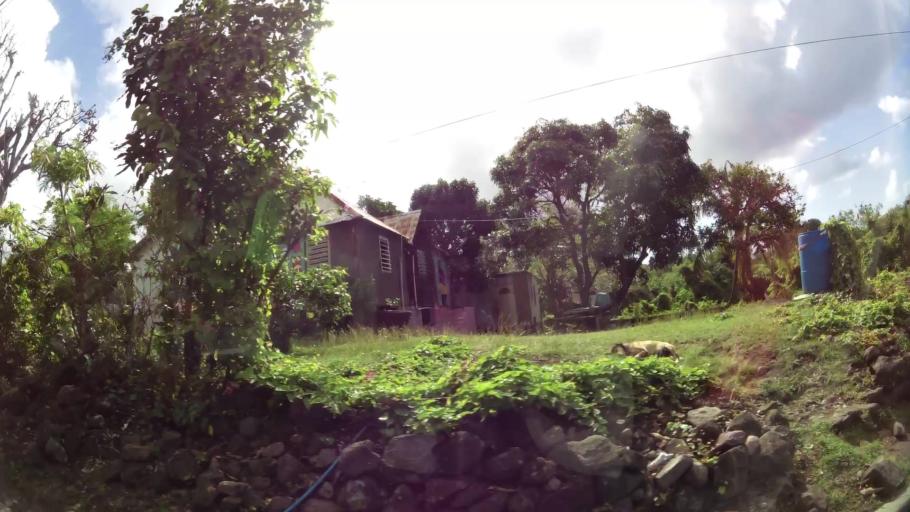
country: KN
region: Saint John Figtree
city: Fig Tree
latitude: 17.1295
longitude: -62.6019
